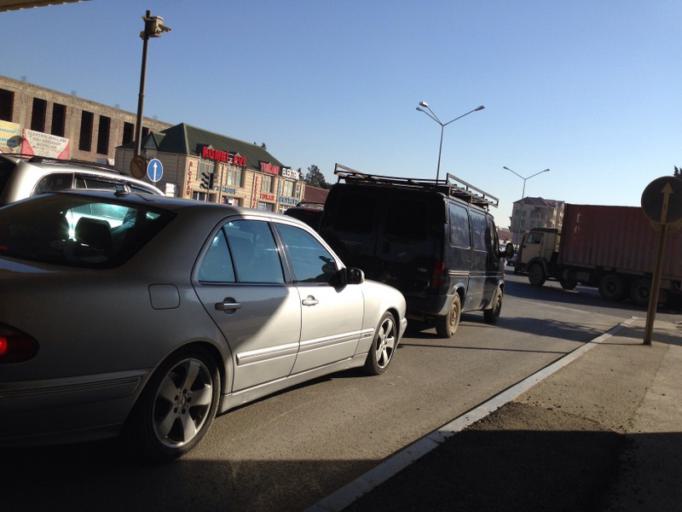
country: AZ
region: Baki
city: Baku
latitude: 40.4158
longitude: 49.8585
